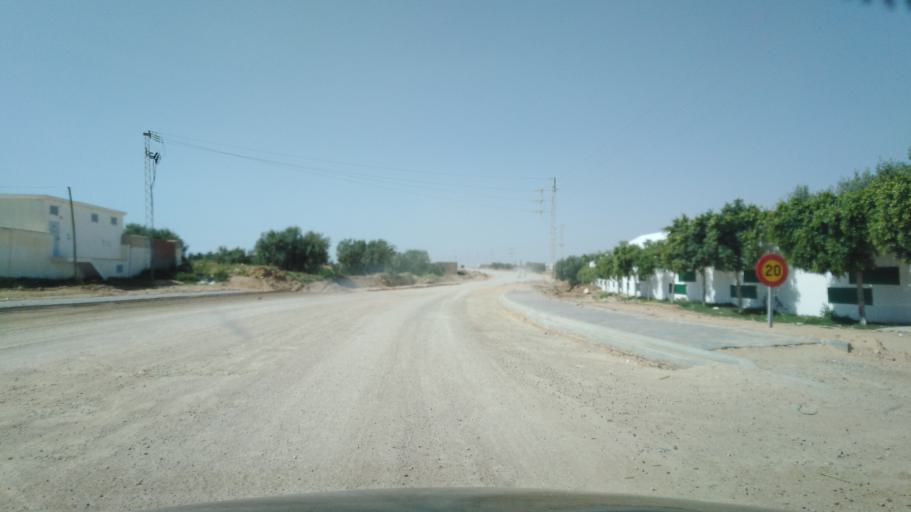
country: TN
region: Safaqis
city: Sfax
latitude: 34.7252
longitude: 10.5129
